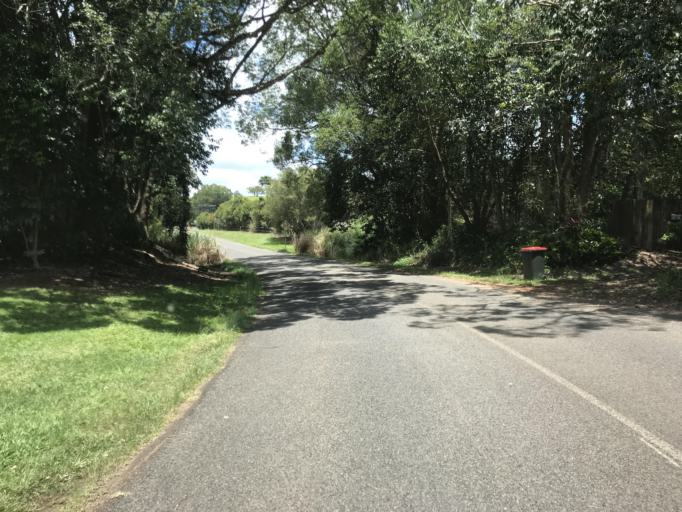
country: AU
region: Queensland
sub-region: Tablelands
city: Atherton
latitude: -17.3460
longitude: 145.5968
